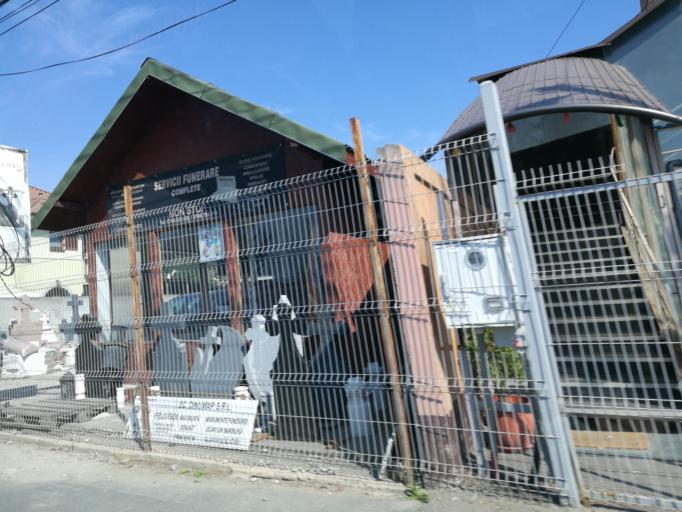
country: RO
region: Ilfov
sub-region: Comuna Otopeni
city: Otopeni
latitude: 44.5501
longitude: 26.0802
